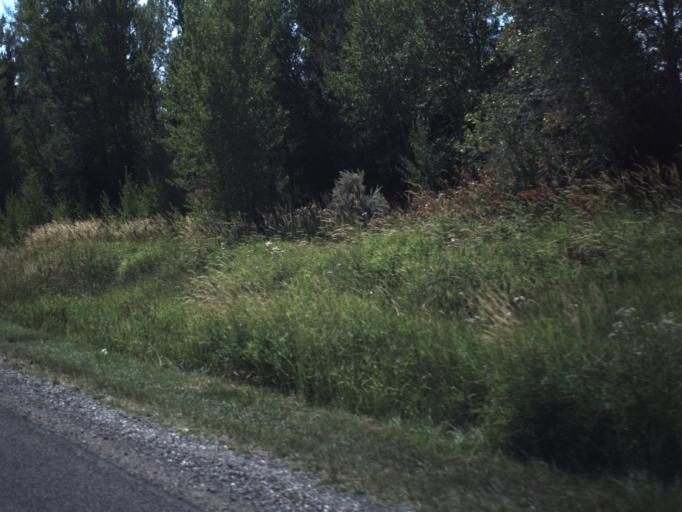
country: US
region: Utah
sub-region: Rich County
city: Randolph
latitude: 41.8581
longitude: -111.3648
